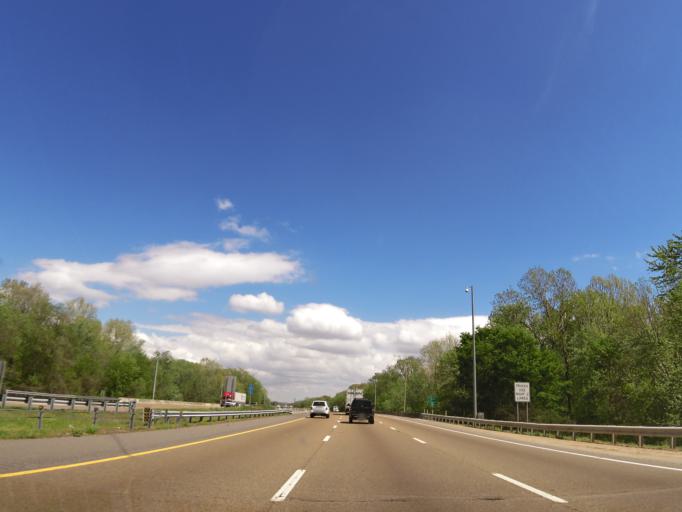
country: US
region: Tennessee
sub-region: Shelby County
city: Bartlett
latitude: 35.1899
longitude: -89.9435
